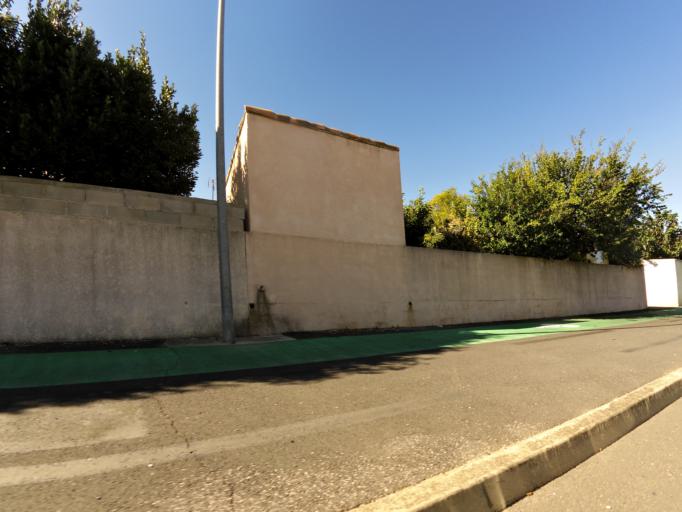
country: FR
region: Languedoc-Roussillon
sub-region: Departement de l'Herault
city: Lunel
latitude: 43.6673
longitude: 4.1335
